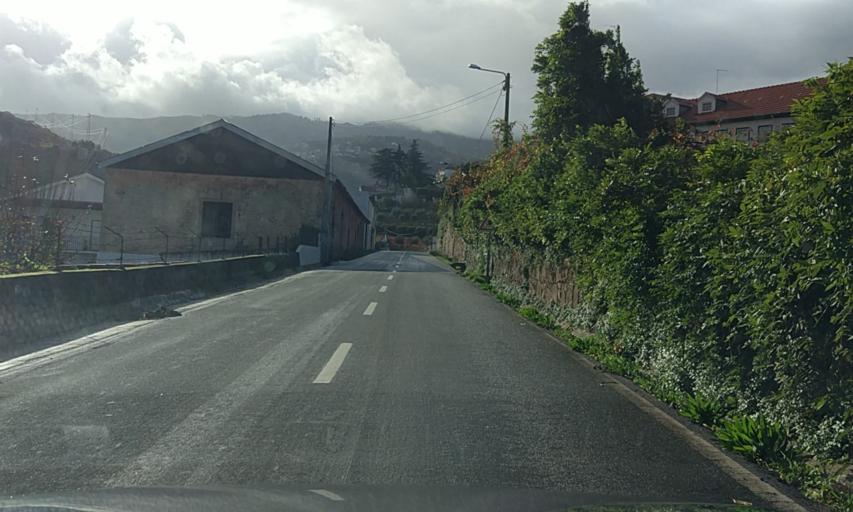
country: PT
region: Vila Real
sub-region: Peso da Regua
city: Peso da Regua
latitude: 41.1312
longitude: -7.7934
